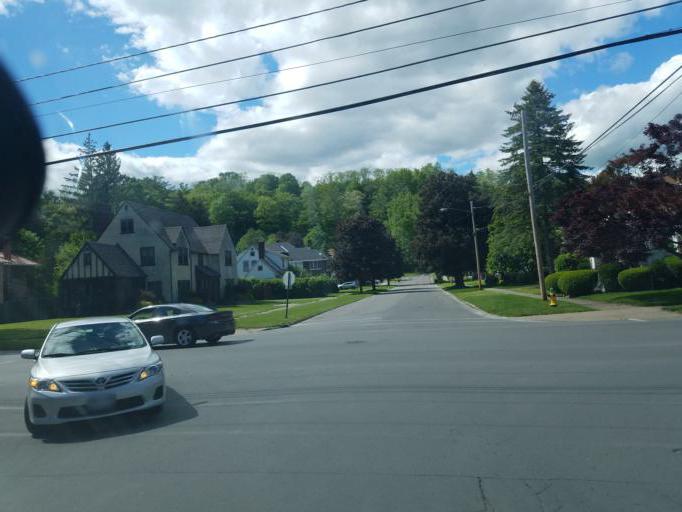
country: US
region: New York
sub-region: Herkimer County
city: Herkimer
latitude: 43.0307
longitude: -74.9909
